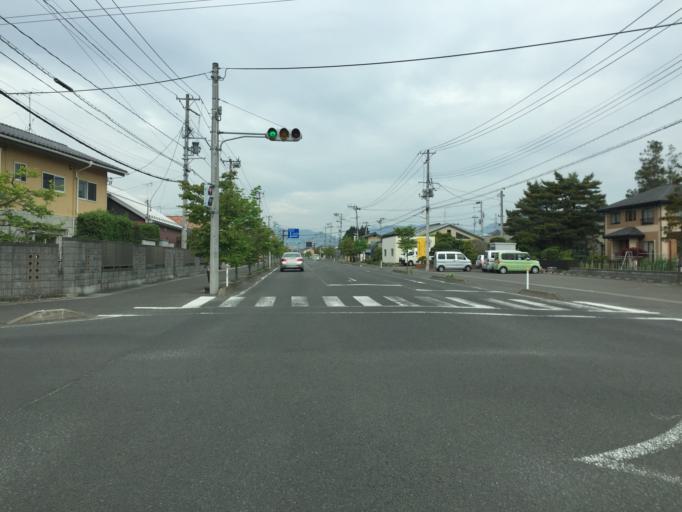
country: JP
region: Fukushima
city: Fukushima-shi
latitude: 37.7850
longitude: 140.4518
